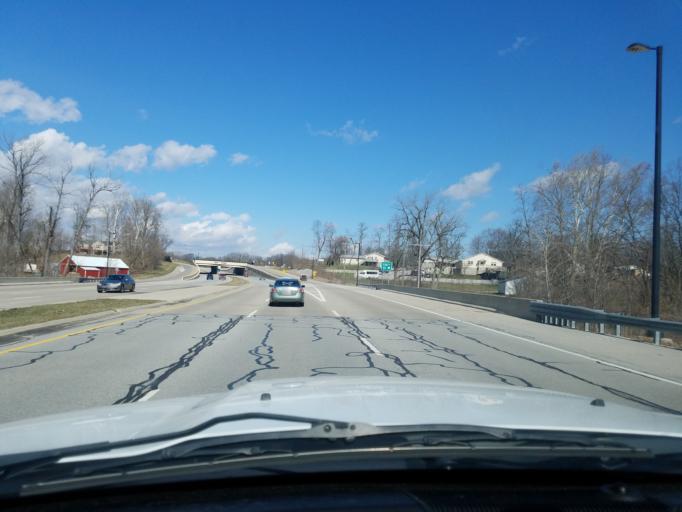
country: US
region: Indiana
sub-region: Hamilton County
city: Carmel
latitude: 39.9831
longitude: -86.1131
